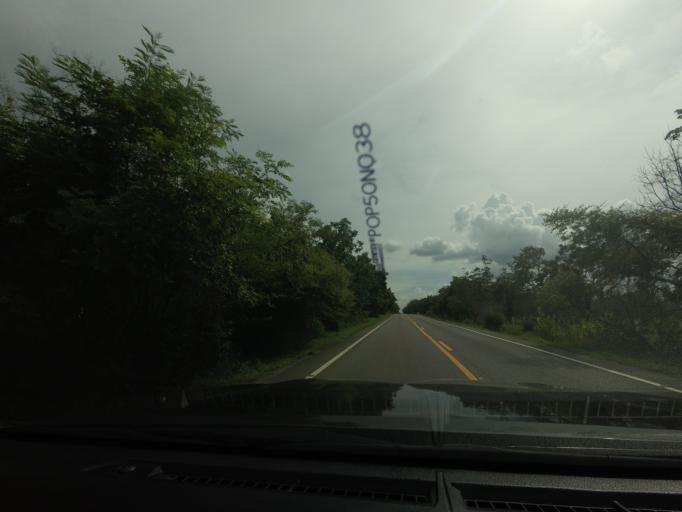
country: TH
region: Kanchanaburi
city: Kanchanaburi
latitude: 14.1454
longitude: 99.4178
